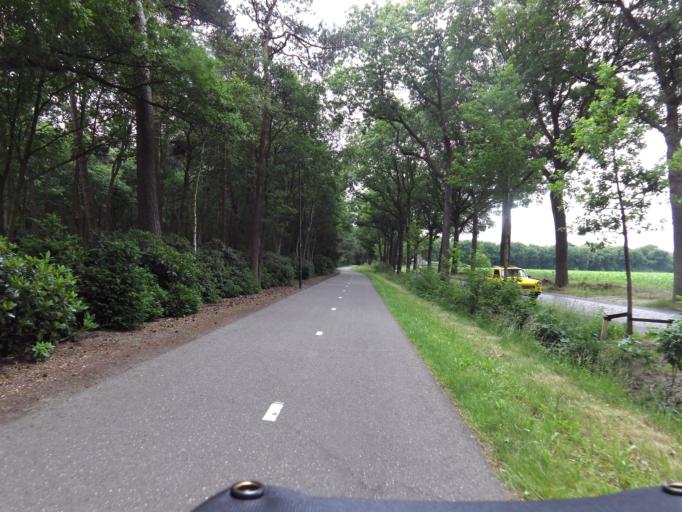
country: NL
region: North Brabant
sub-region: Gemeente Bladel en Netersel
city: Bladel
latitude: 51.3975
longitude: 5.2063
